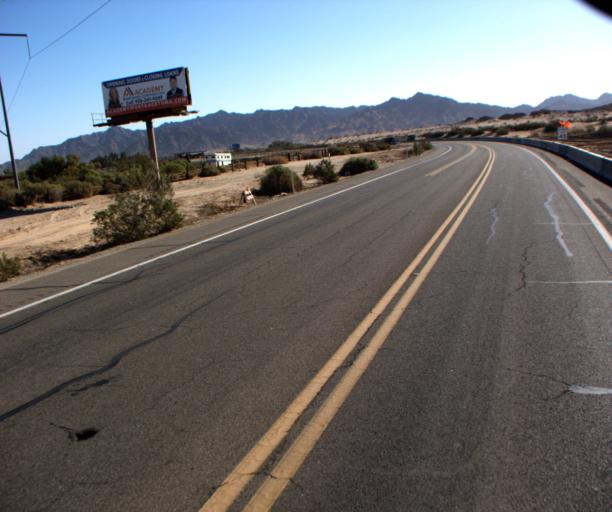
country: US
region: Arizona
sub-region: Yuma County
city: Fortuna Foothills
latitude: 32.6998
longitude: -114.4443
